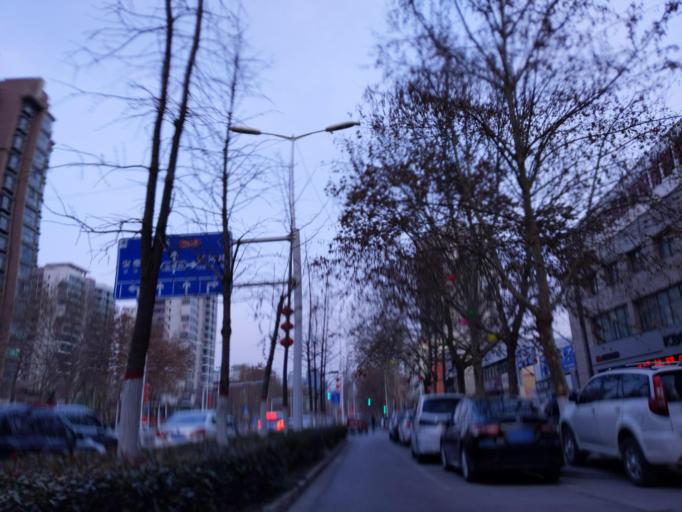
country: CN
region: Henan Sheng
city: Puyang
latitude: 35.7806
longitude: 115.0316
